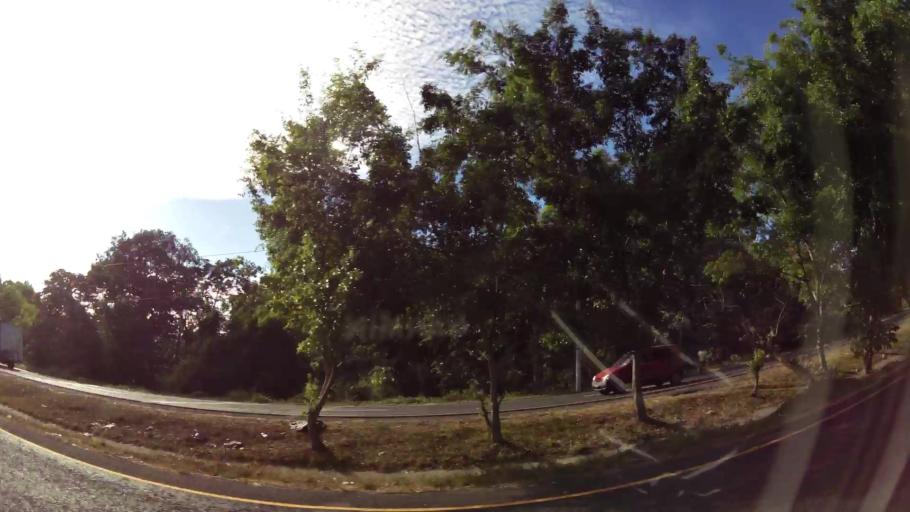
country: SV
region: Cuscatlan
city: Tecoluca
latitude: 13.7401
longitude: -89.0381
